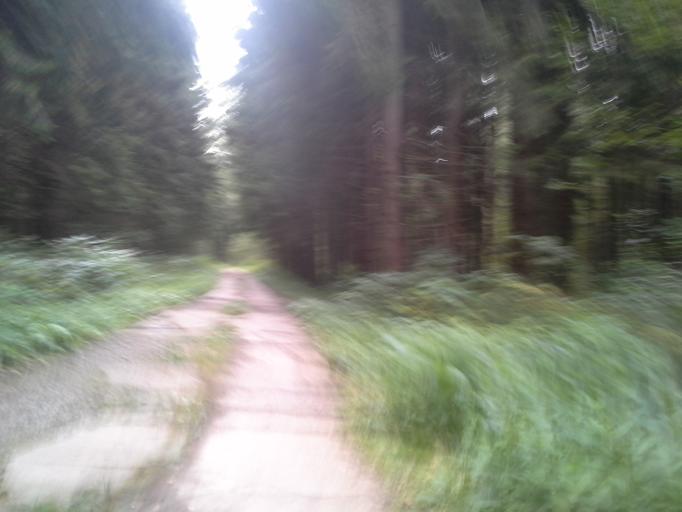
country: RU
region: Moskovskaya
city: Vatutinki
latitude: 55.5249
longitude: 37.3362
